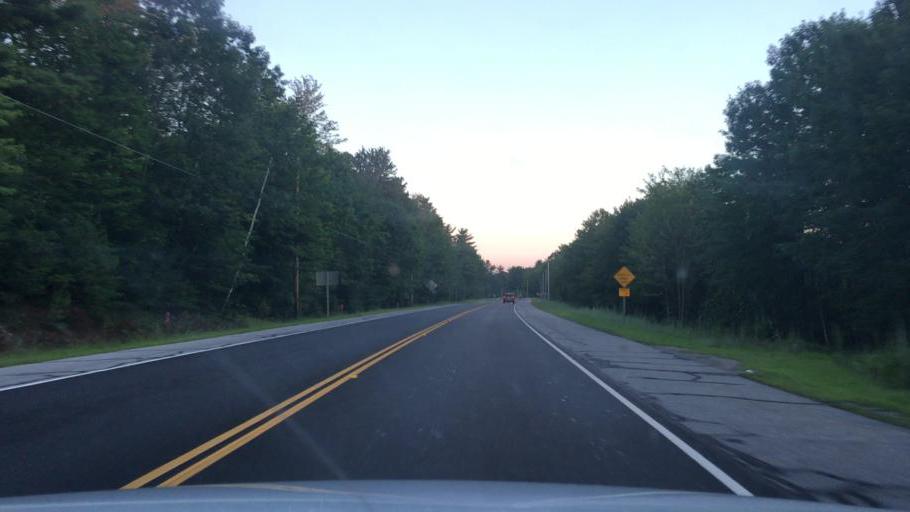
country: US
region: Maine
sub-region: Androscoggin County
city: Turner
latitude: 44.2489
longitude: -70.2596
